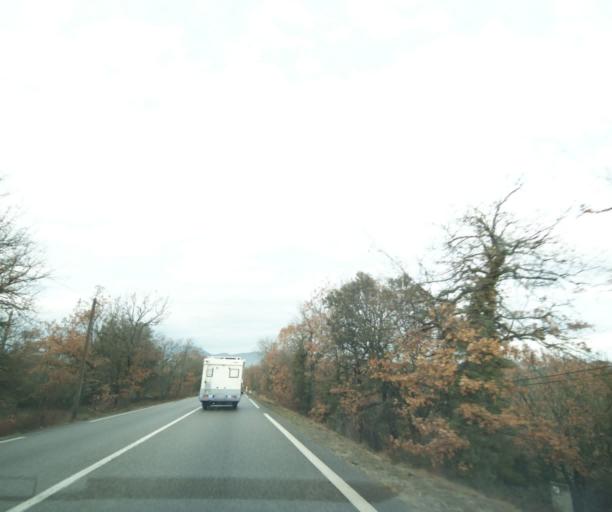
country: FR
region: Provence-Alpes-Cote d'Azur
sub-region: Departement du Var
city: Tourves
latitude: 43.4250
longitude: 5.9026
